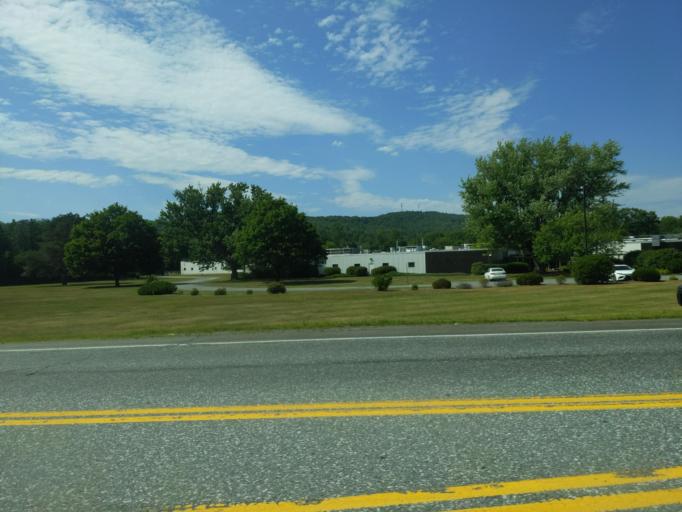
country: US
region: New Hampshire
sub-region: Grafton County
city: Lebanon
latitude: 43.6370
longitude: -72.2856
